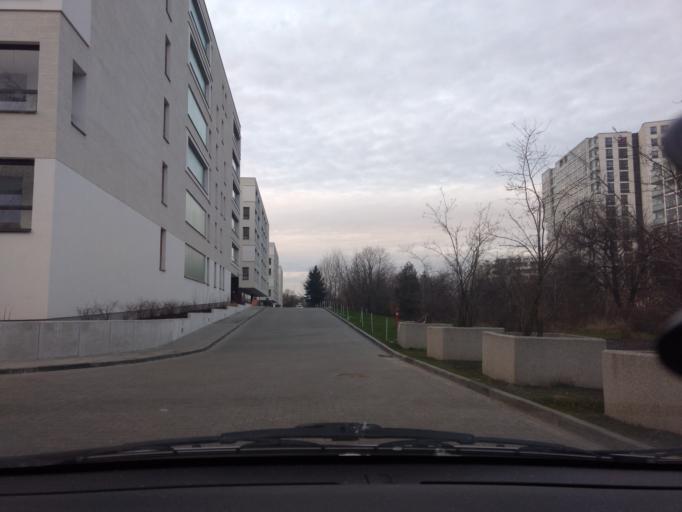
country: PL
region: Masovian Voivodeship
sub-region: Warszawa
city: Praga Poludnie
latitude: 52.2277
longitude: 21.0750
